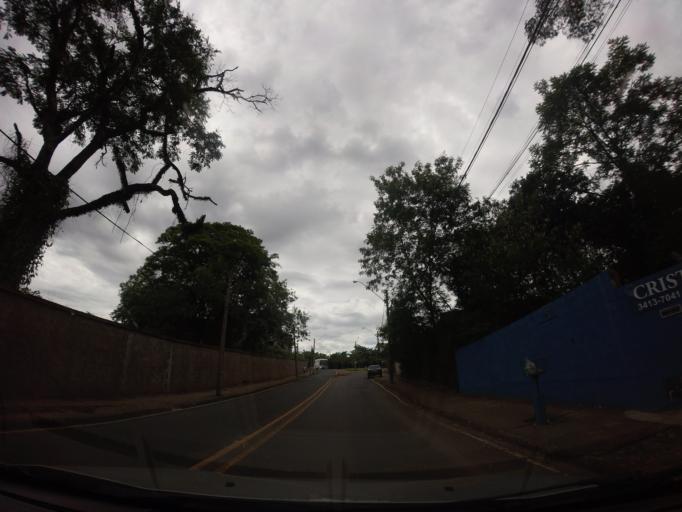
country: BR
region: Sao Paulo
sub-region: Piracicaba
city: Piracicaba
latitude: -22.7498
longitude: -47.6154
